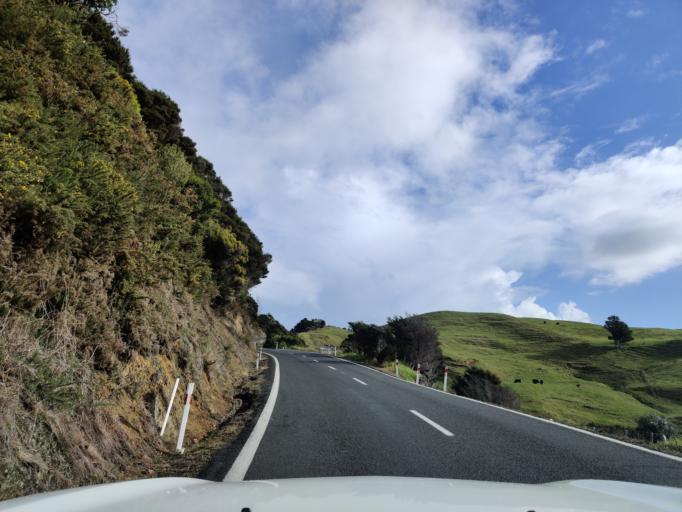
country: NZ
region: Waikato
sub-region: Thames-Coromandel District
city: Coromandel
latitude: -36.8161
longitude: 175.4849
